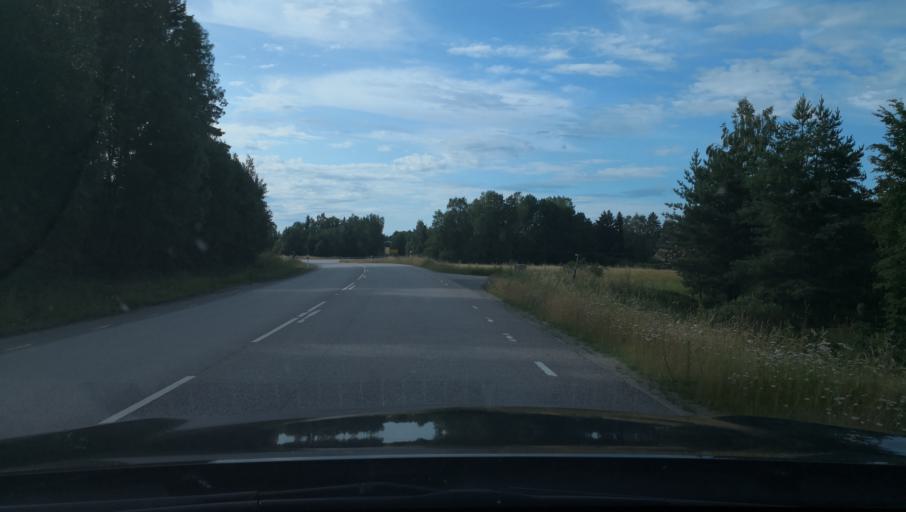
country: SE
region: Uppsala
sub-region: Habo Kommun
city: Balsta
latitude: 59.6062
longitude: 17.5052
